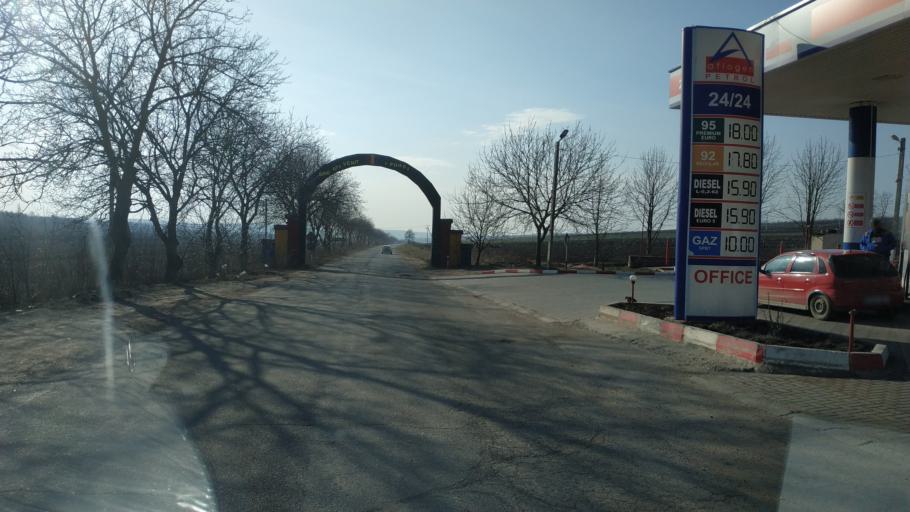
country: MD
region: Chisinau
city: Singera
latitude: 46.8560
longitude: 29.0210
